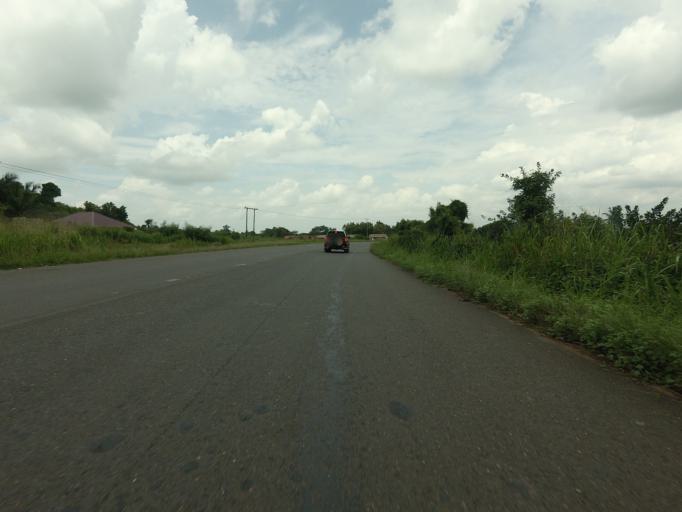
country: GH
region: Volta
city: Ho
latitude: 6.4216
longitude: 0.1716
